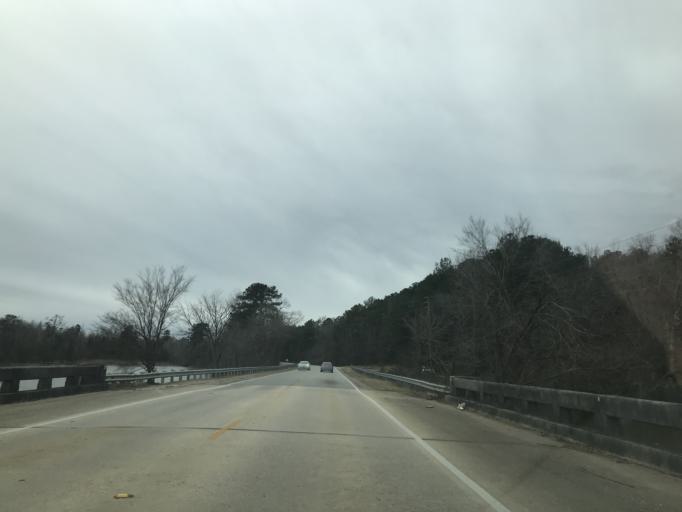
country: US
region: Alabama
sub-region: Shelby County
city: Brook Highland
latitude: 33.4481
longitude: -86.6548
